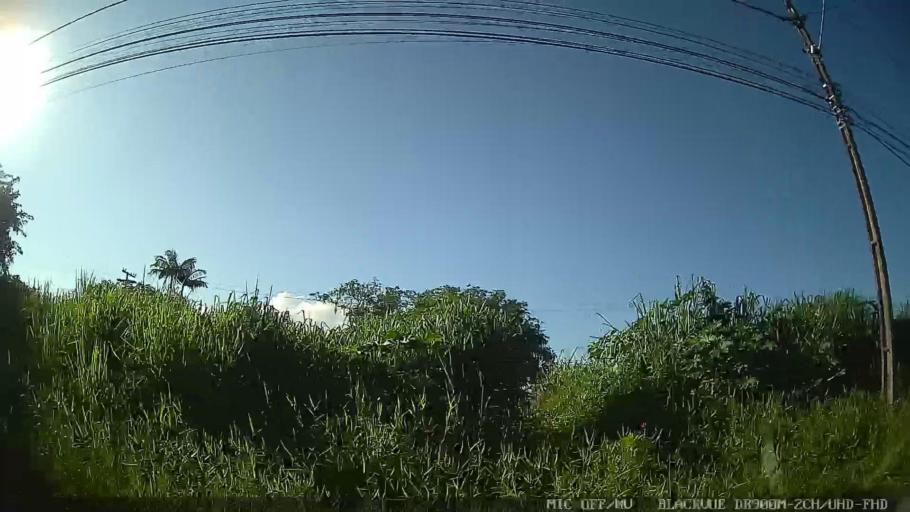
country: BR
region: Sao Paulo
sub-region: Peruibe
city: Peruibe
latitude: -24.2739
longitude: -46.9509
